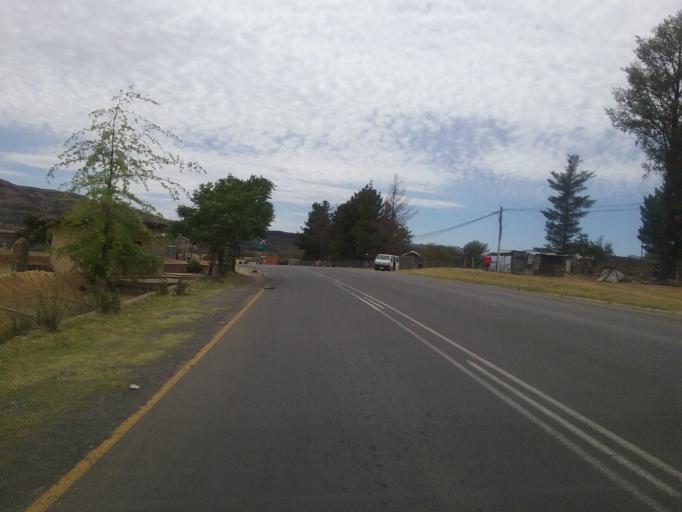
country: LS
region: Maseru
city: Nako
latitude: -29.6238
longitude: 27.4947
